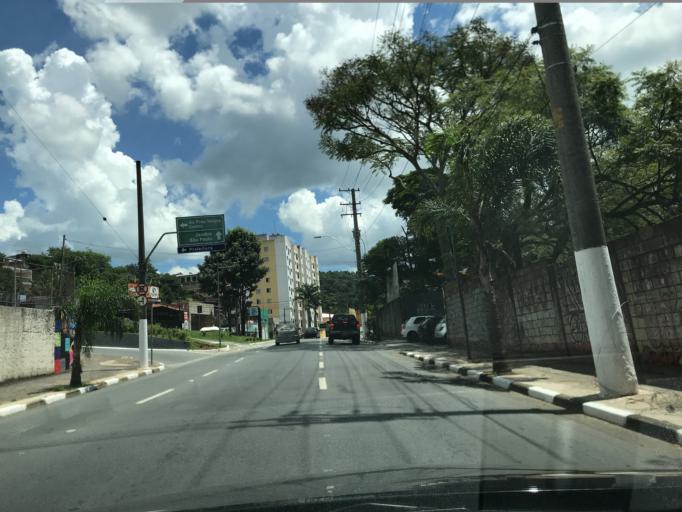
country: BR
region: Sao Paulo
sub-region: Itapevi
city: Itapevi
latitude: -23.5369
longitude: -46.9389
